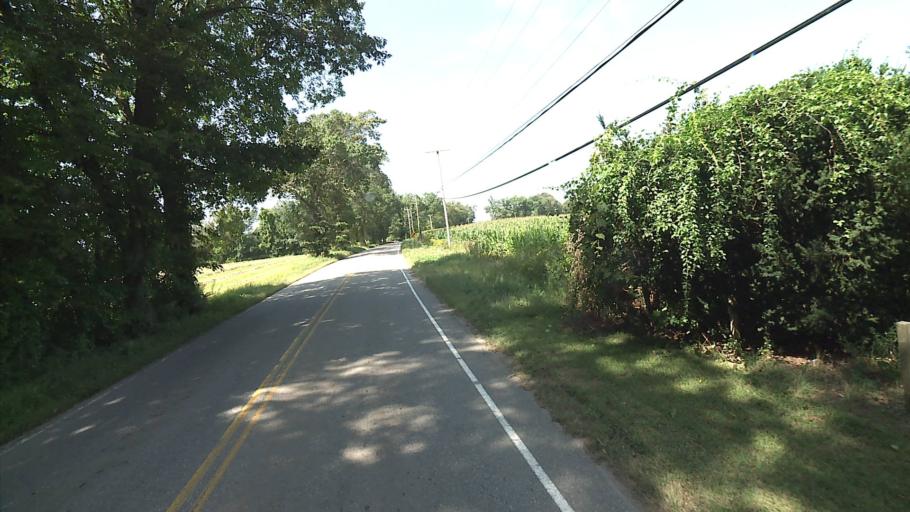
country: US
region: Connecticut
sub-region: Windham County
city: South Windham
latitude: 41.6178
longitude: -72.1959
